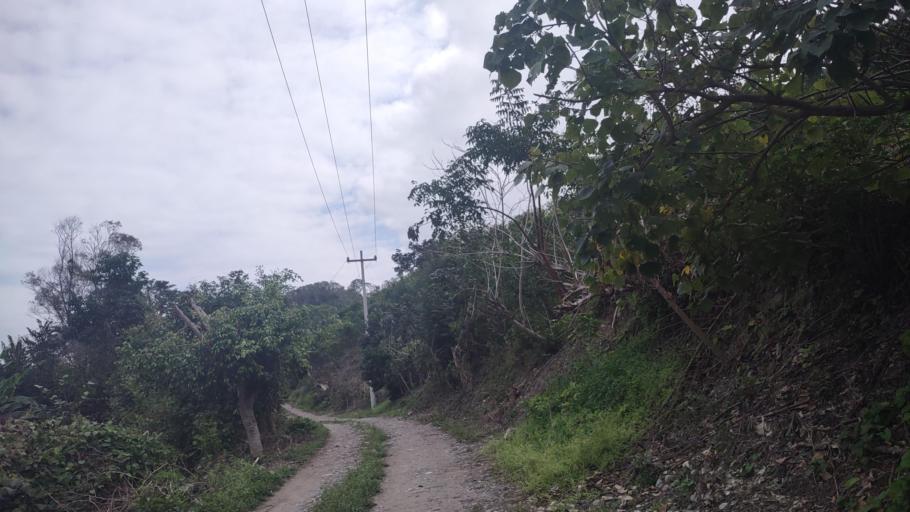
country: MX
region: Veracruz
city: Papantla de Olarte
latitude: 20.4343
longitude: -97.2620
